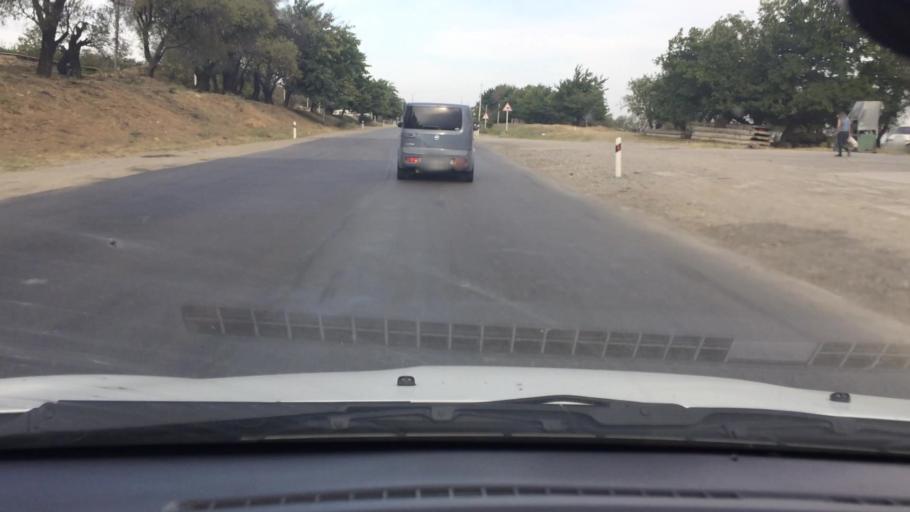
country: GE
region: T'bilisi
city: Tbilisi
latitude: 41.6408
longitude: 44.8343
